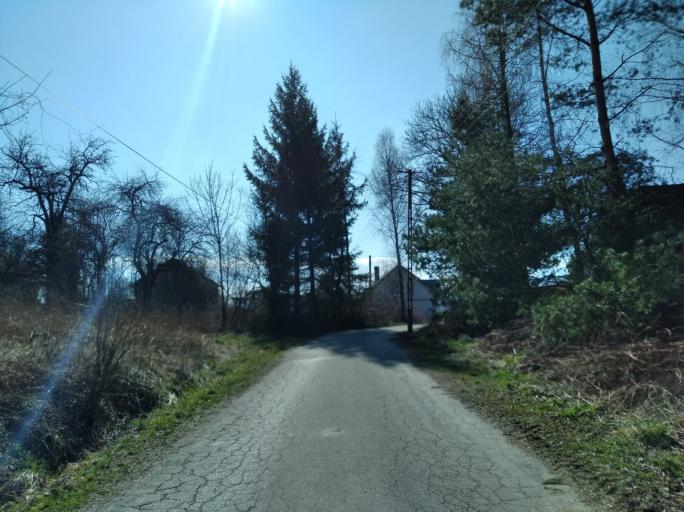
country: PL
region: Subcarpathian Voivodeship
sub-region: Powiat strzyzowski
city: Wysoka Strzyzowska
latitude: 49.8307
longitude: 21.7454
